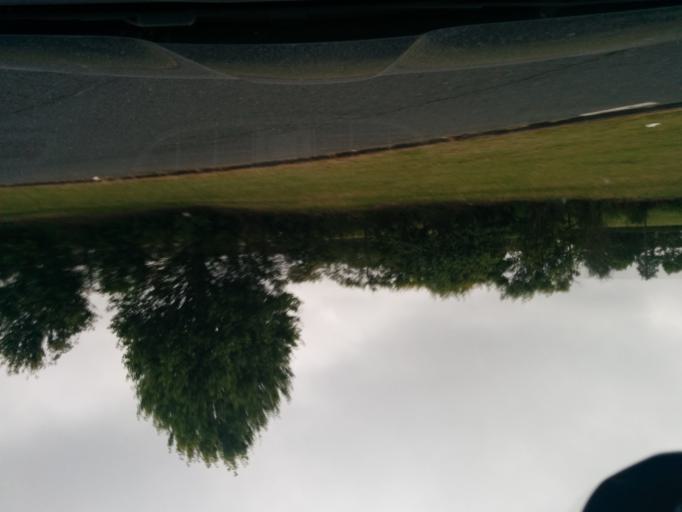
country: GB
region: England
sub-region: Northumberland
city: Cramlington
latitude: 55.0957
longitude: -1.5783
